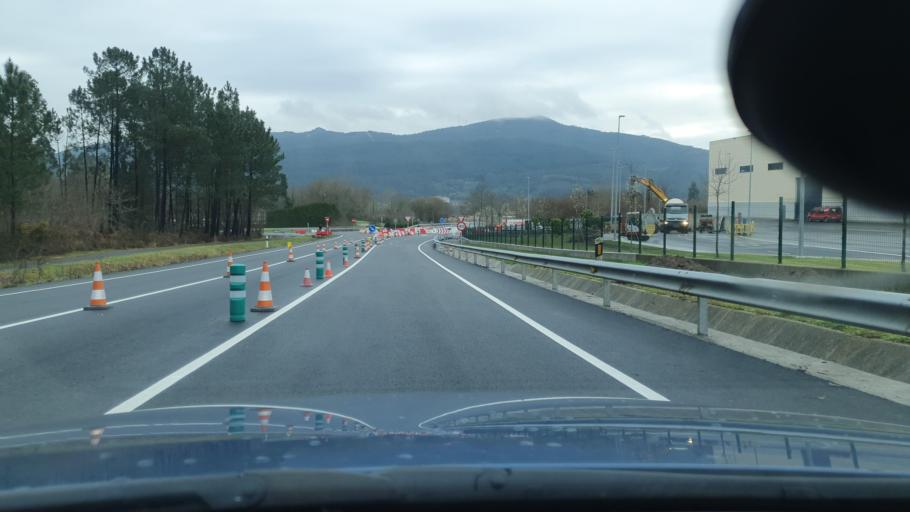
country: ES
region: Galicia
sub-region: Provincia da Coruna
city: Padron
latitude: 42.7571
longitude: -8.6719
